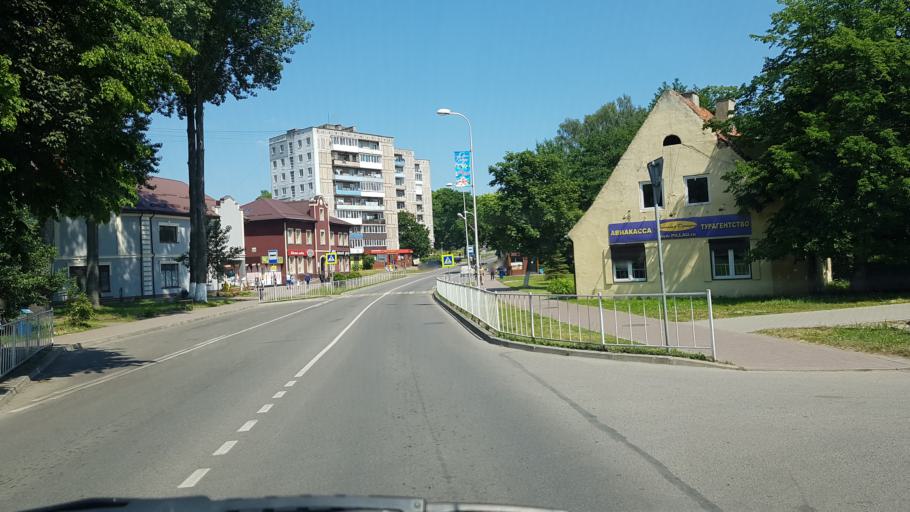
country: RU
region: Kaliningrad
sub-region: Gorod Kaliningrad
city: Baltiysk
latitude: 54.6509
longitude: 19.9067
